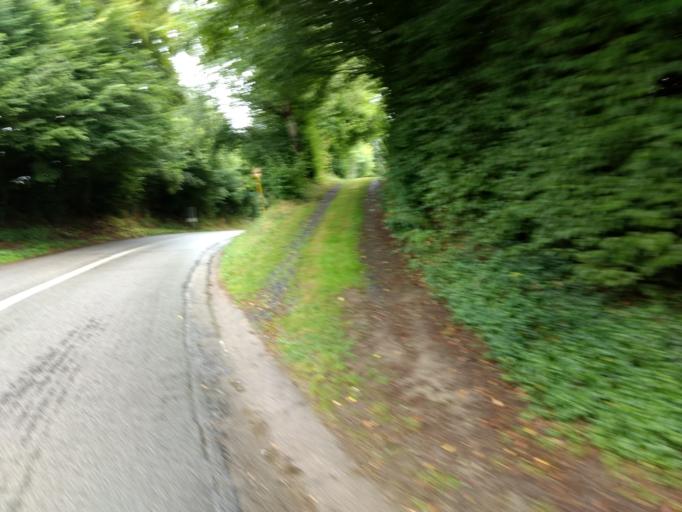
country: BE
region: Wallonia
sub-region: Province du Luxembourg
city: Houffalize
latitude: 50.1470
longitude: 5.7188
